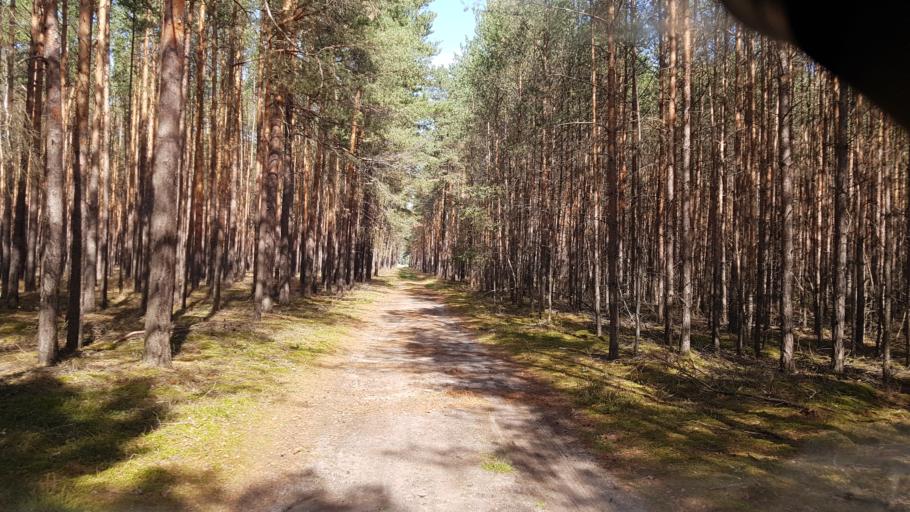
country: DE
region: Brandenburg
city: Sonnewalde
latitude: 51.6539
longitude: 13.6390
